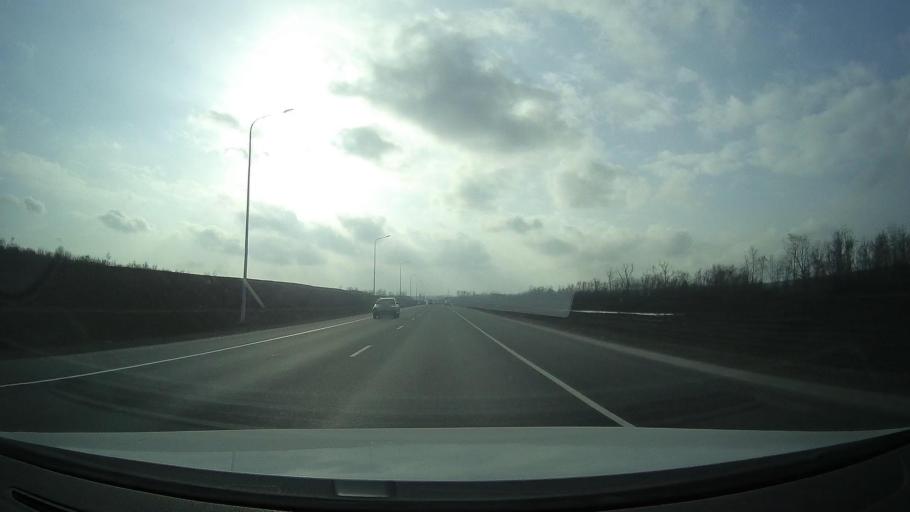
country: RU
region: Rostov
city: Grushevskaya
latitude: 47.4245
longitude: 39.8645
